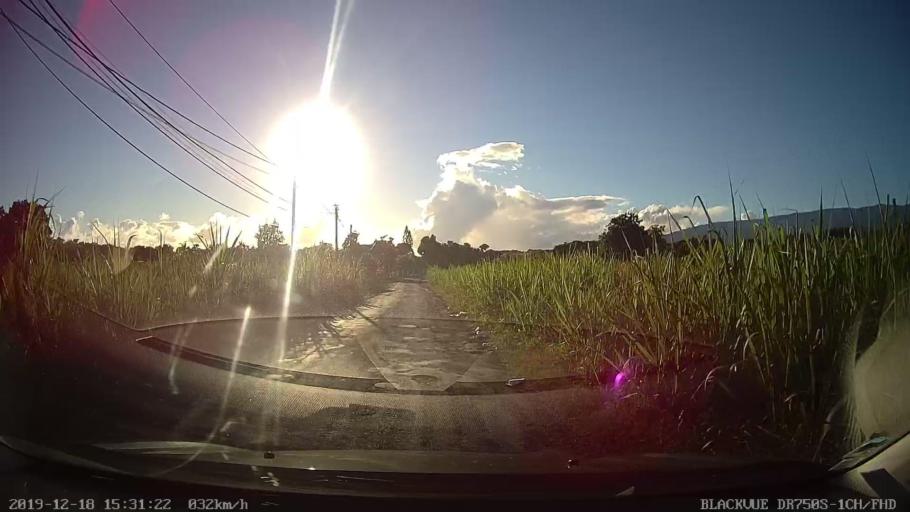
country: RE
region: Reunion
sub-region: Reunion
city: Bras-Panon
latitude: -21.0008
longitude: 55.6684
